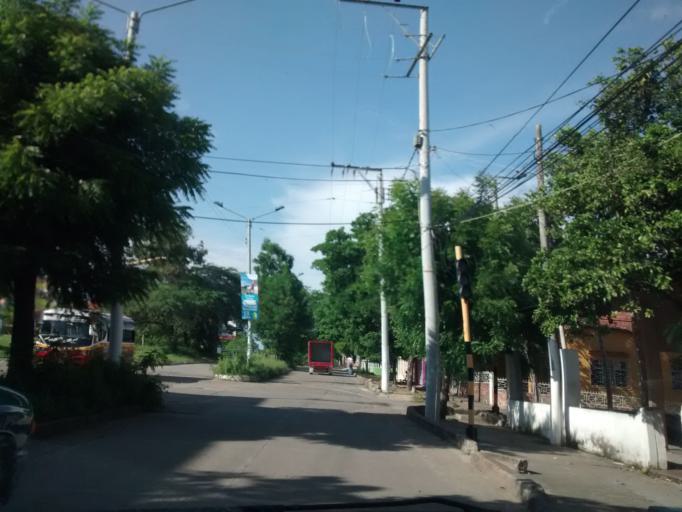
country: CO
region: Cundinamarca
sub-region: Girardot
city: Girardot City
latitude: 4.3165
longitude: -74.7915
